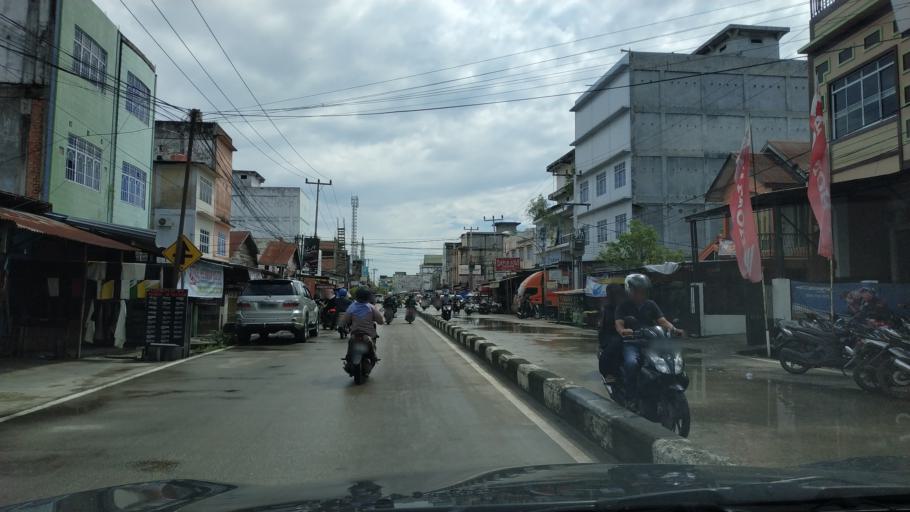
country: ID
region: Riau
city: Tembilahan
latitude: -0.3233
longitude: 103.1501
